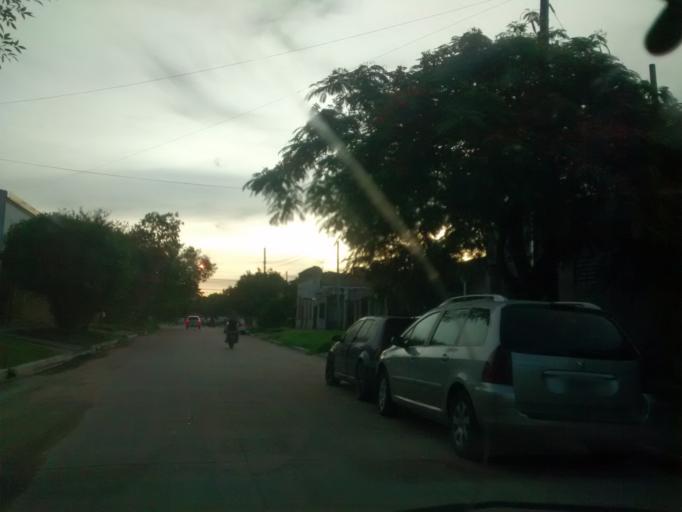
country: AR
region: Chaco
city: Resistencia
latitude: -27.4370
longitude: -58.9939
